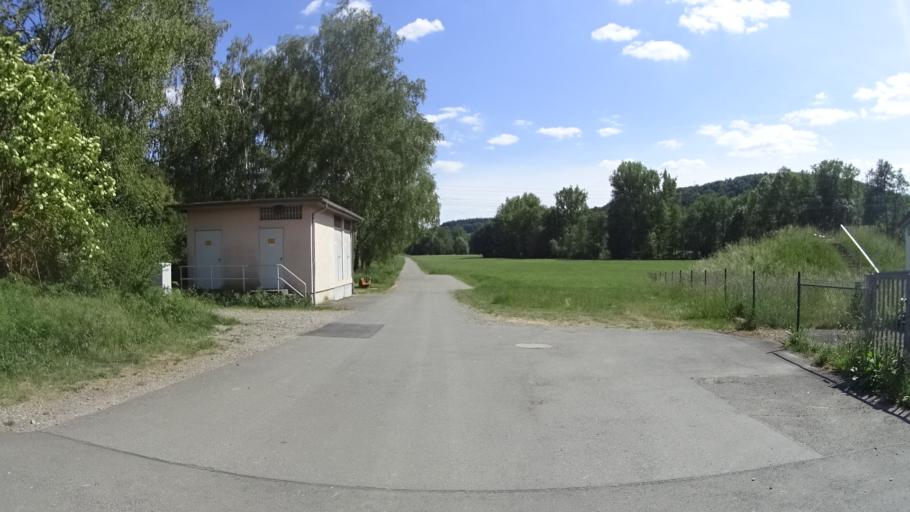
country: DE
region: Baden-Wuerttemberg
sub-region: Karlsruhe Region
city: Hardheim
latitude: 49.6005
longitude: 9.4781
